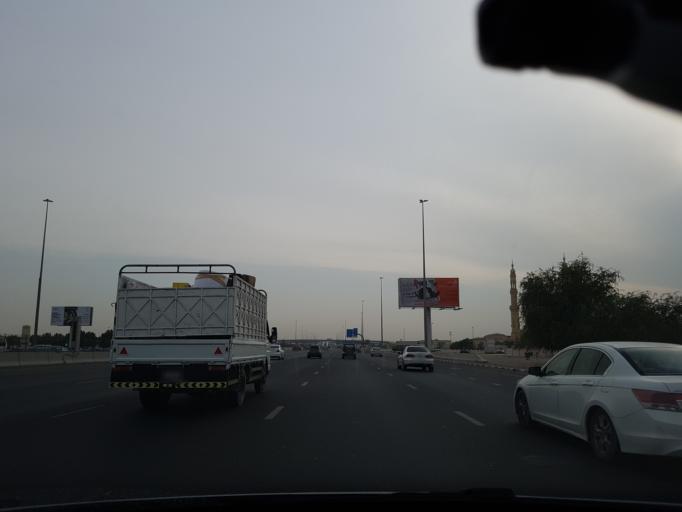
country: AE
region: Ash Shariqah
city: Sharjah
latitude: 25.3450
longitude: 55.4727
